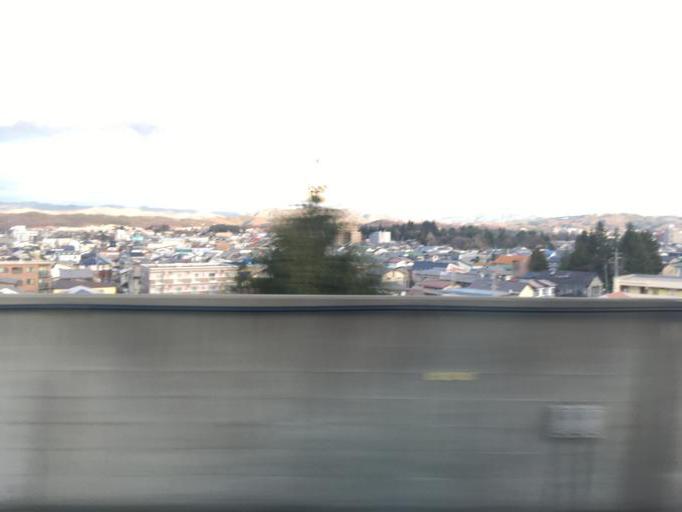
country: JP
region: Iwate
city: Morioka-shi
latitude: 39.7215
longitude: 141.1174
